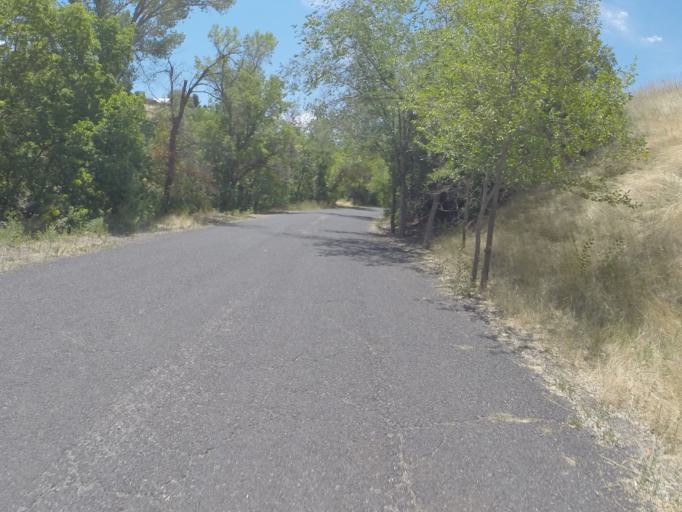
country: US
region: Utah
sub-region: Salt Lake County
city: Salt Lake City
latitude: 40.7831
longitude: -111.8837
